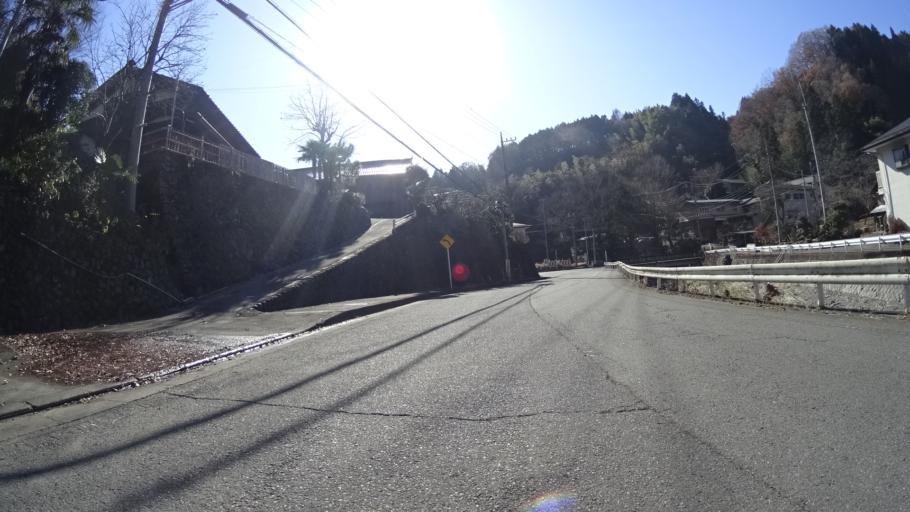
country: JP
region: Yamanashi
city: Uenohara
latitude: 35.6344
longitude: 139.1414
